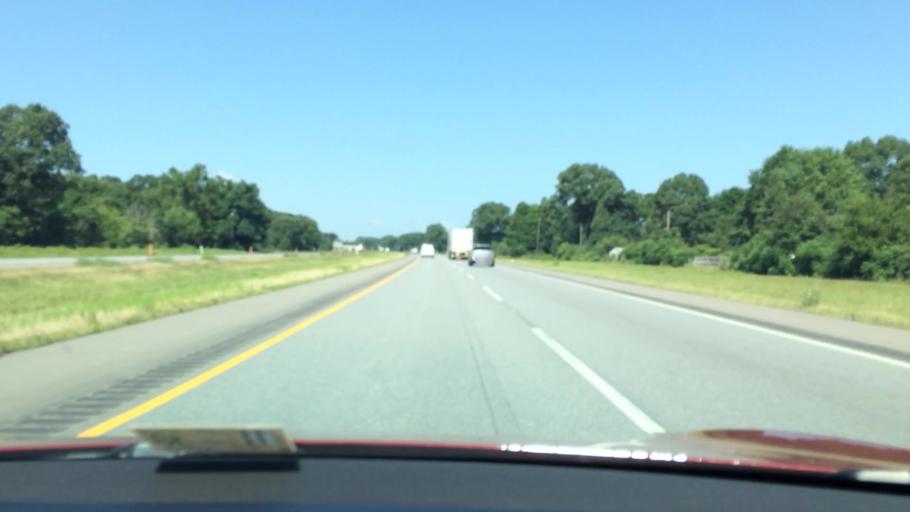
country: US
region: Indiana
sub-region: Elkhart County
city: Simonton Lake
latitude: 41.7330
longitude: -86.0251
